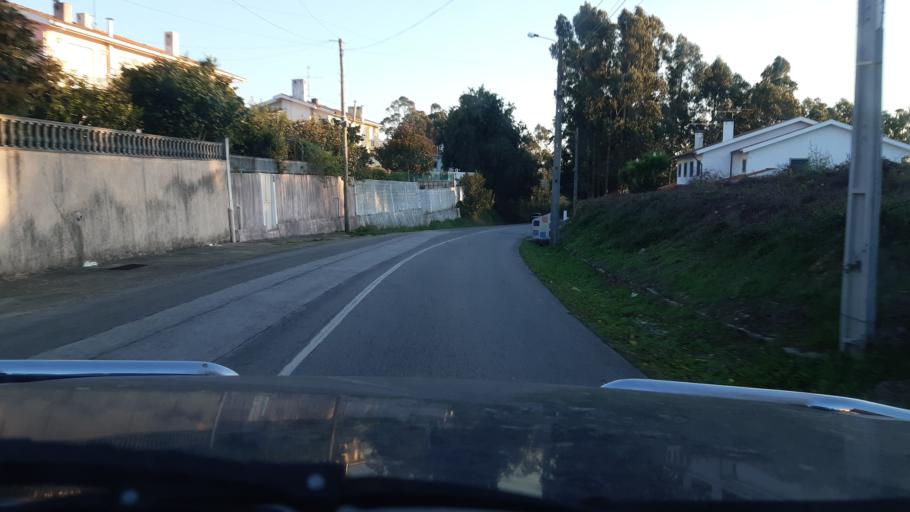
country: PT
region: Aveiro
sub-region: Agueda
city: Agueda
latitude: 40.5798
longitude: -8.4633
